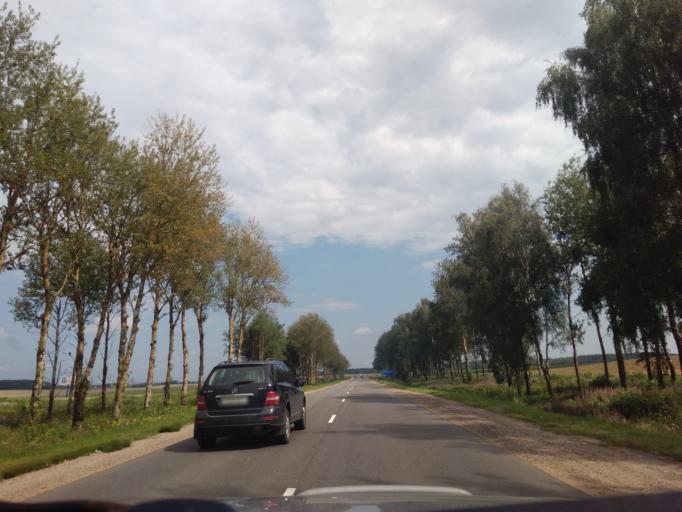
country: BY
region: Minsk
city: Khatsyezhyna
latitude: 53.9119
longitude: 27.3388
